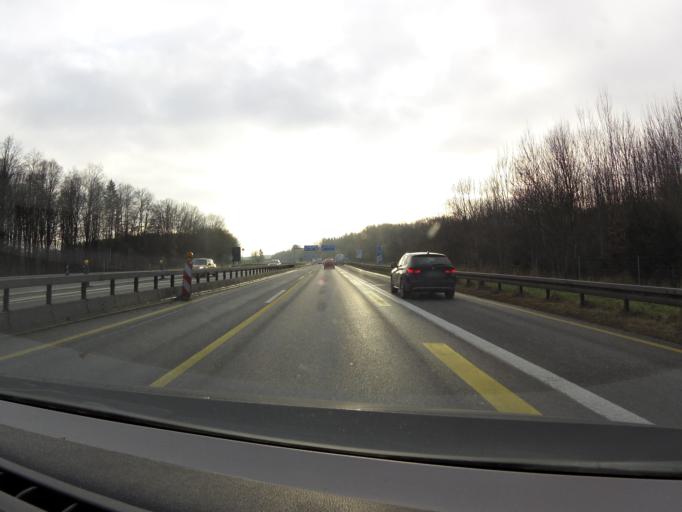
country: DE
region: Bavaria
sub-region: Upper Bavaria
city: Schaftlarn
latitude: 48.0255
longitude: 11.4230
